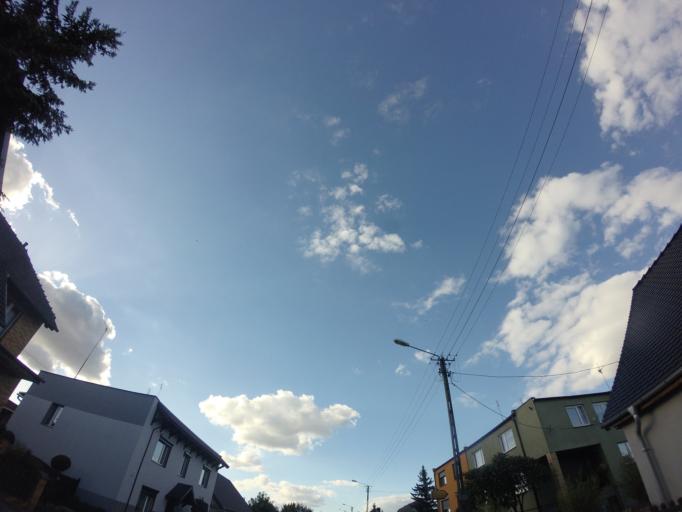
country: PL
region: Greater Poland Voivodeship
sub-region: Powiat nowotomyski
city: Nowy Tomysl
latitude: 52.2658
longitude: 16.1354
